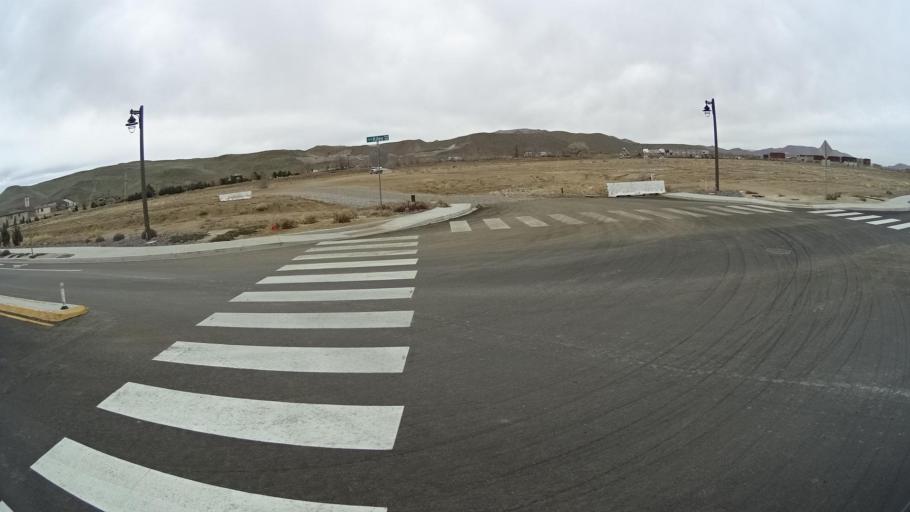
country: US
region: Nevada
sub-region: Washoe County
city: Spanish Springs
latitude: 39.6039
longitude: -119.7218
